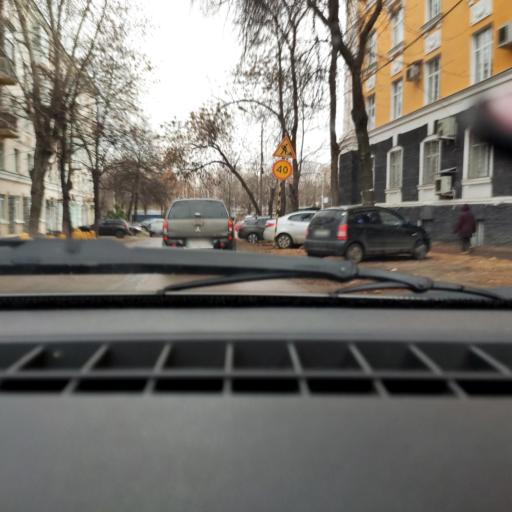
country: RU
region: Bashkortostan
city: Ufa
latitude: 54.7410
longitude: 55.9469
